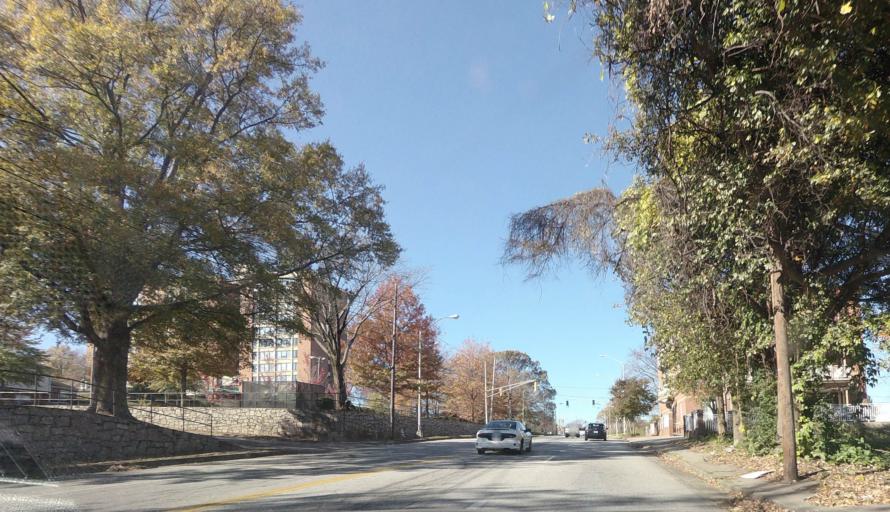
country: US
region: Georgia
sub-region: Fulton County
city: Atlanta
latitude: 33.7421
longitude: -84.3963
